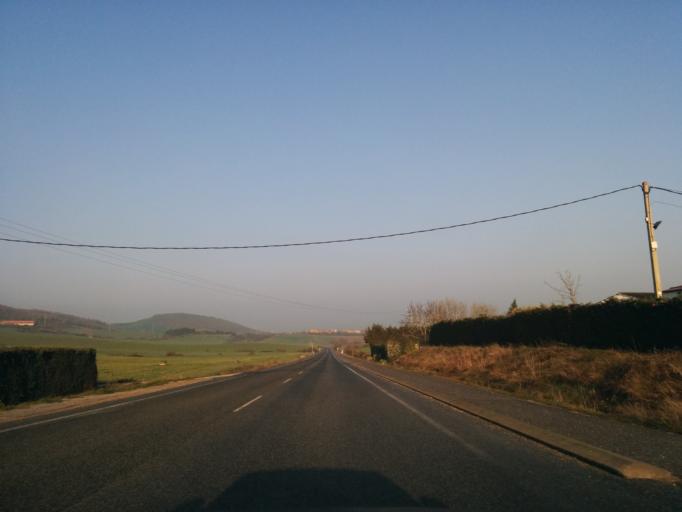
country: ES
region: Navarre
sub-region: Provincia de Navarra
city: Elorz
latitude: 42.7628
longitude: -1.5638
